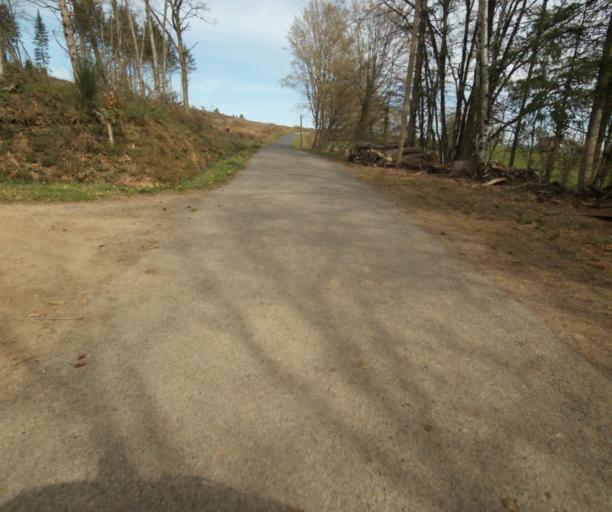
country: FR
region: Limousin
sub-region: Departement de la Correze
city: Correze
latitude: 45.3662
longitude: 1.8195
